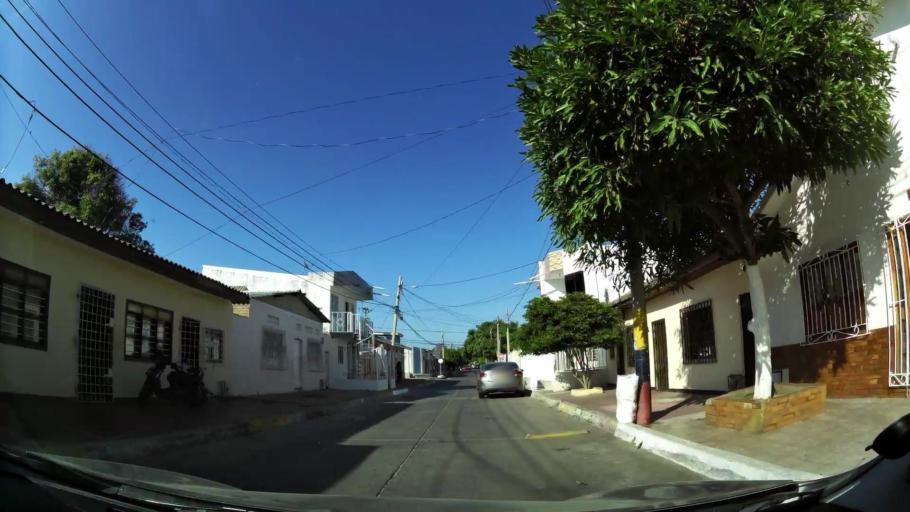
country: CO
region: Atlantico
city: Barranquilla
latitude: 10.9626
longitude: -74.7859
